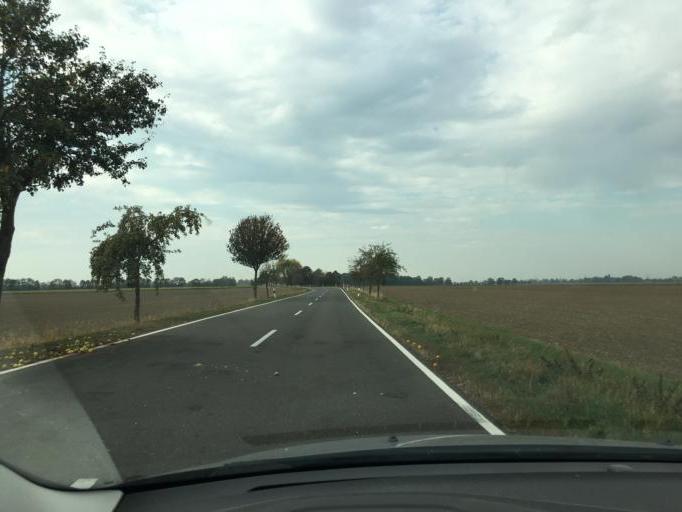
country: DE
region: Saxony
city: Zwochau
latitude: 51.4994
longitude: 12.2559
